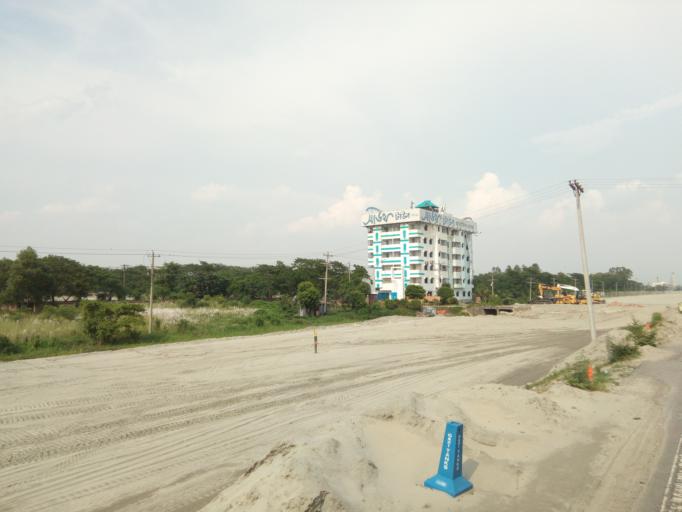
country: BD
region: Dhaka
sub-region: Dhaka
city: Dhaka
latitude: 23.6615
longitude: 90.3723
